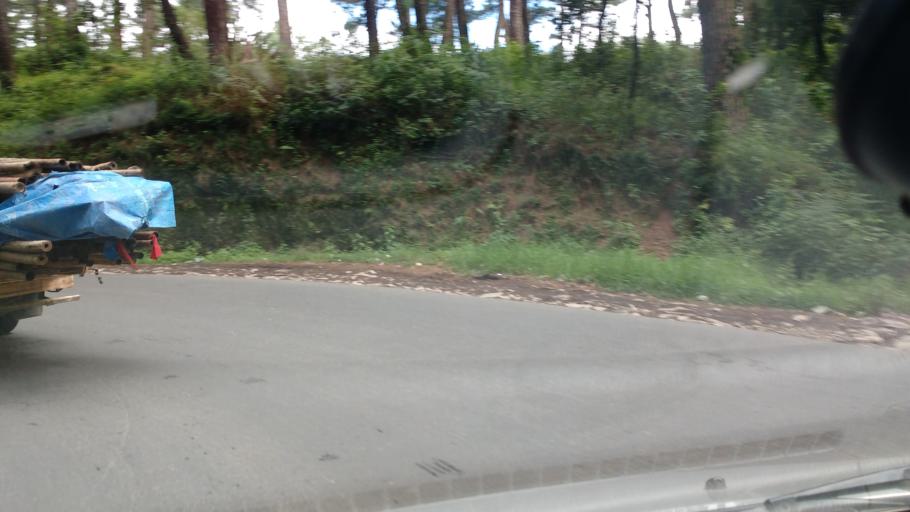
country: IN
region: Meghalaya
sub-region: East Khasi Hills
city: Shillong
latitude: 25.5652
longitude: 91.8592
